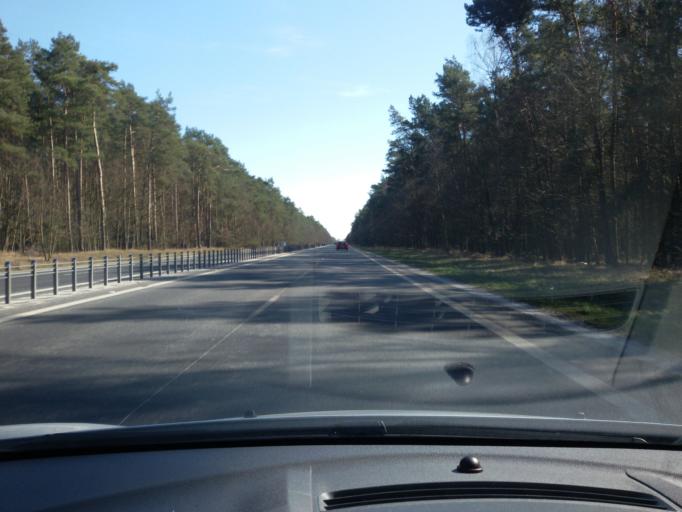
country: PL
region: Greater Poland Voivodeship
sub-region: Powiat leszczynski
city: Rydzyna
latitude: 51.8154
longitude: 16.6231
